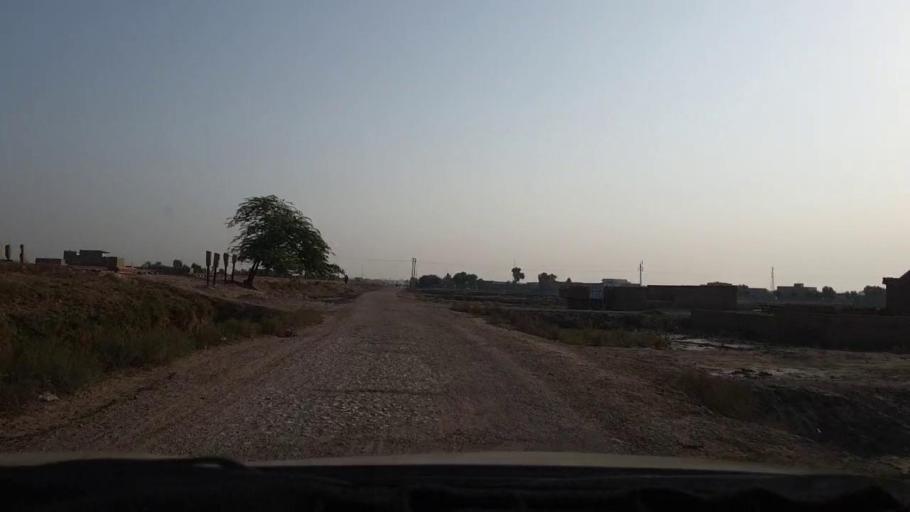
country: PK
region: Sindh
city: Larkana
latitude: 27.5264
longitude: 68.1965
